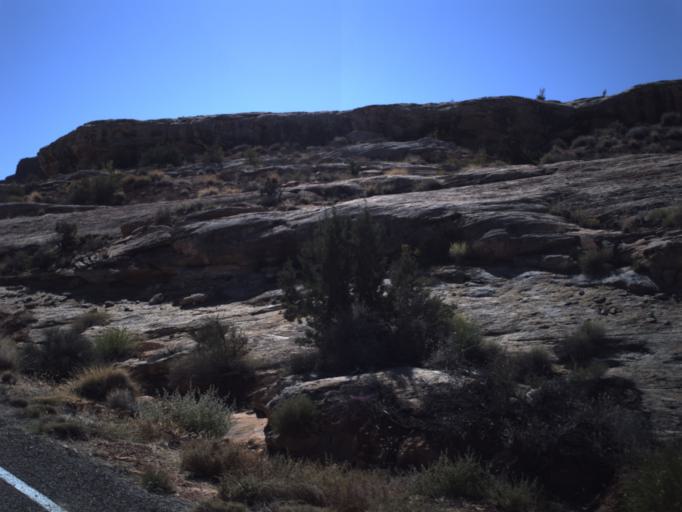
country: US
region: Utah
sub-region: San Juan County
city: Blanding
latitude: 37.8844
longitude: -110.3625
